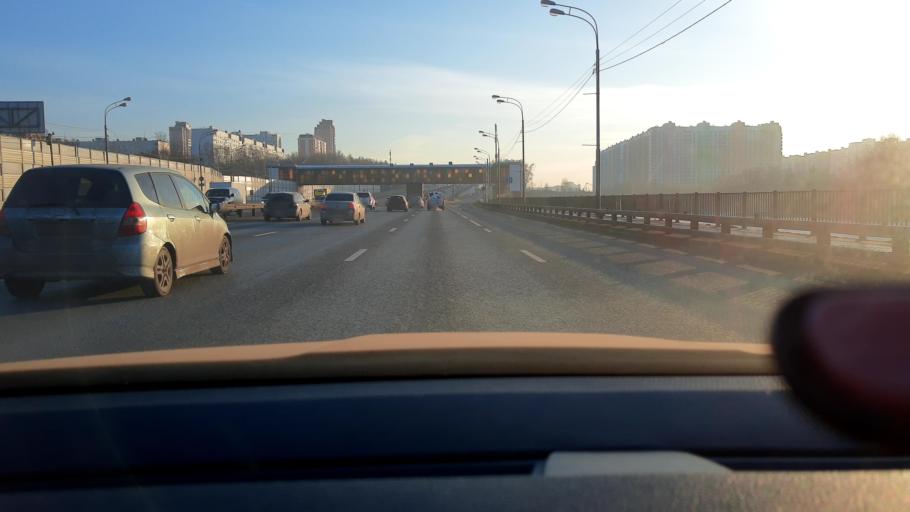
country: RU
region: Moscow
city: Severnyy
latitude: 55.9386
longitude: 37.5448
